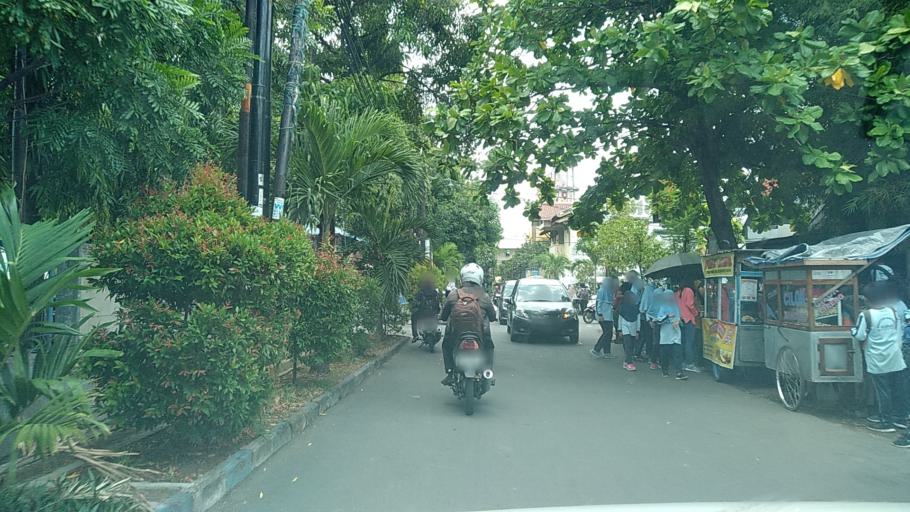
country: ID
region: Central Java
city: Semarang
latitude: -6.9803
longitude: 110.4083
